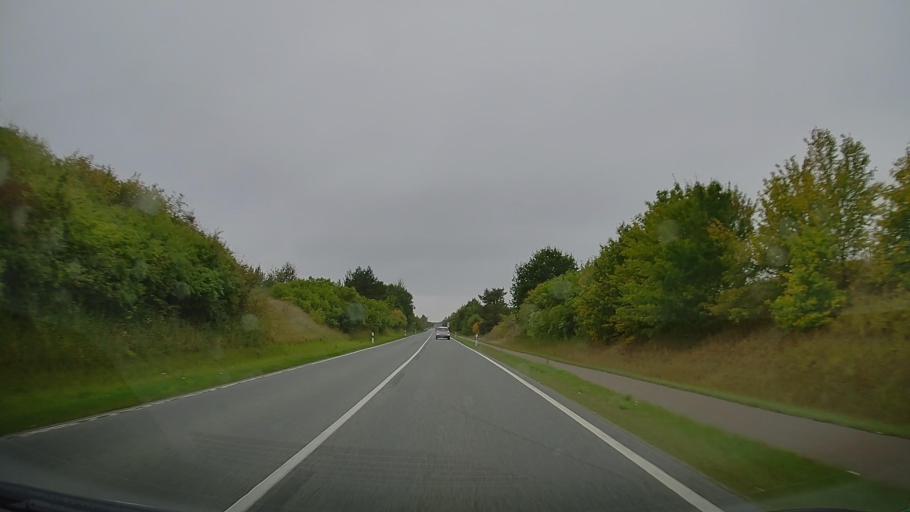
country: DE
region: Mecklenburg-Vorpommern
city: Bruel
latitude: 53.7256
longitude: 11.7259
